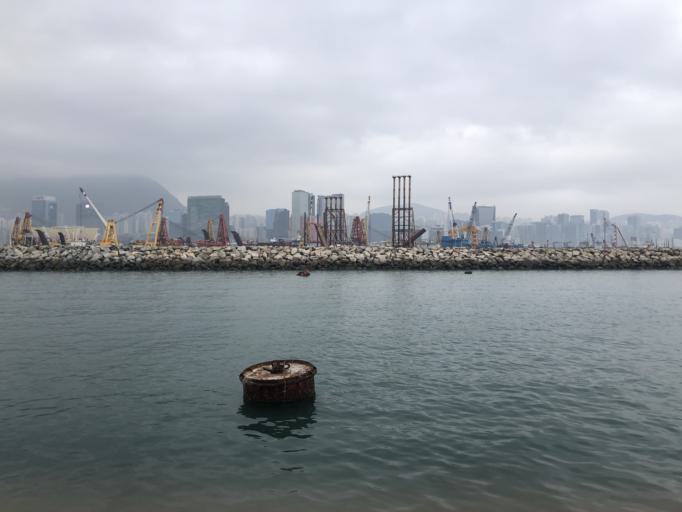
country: HK
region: Kowloon City
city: Kowloon
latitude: 22.3129
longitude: 114.1940
